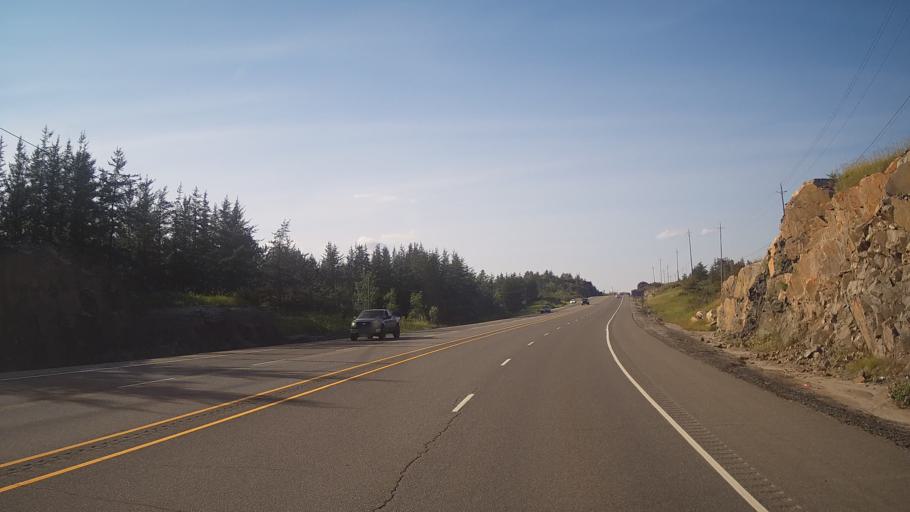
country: CA
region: Ontario
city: Greater Sudbury
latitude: 46.5098
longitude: -81.0519
